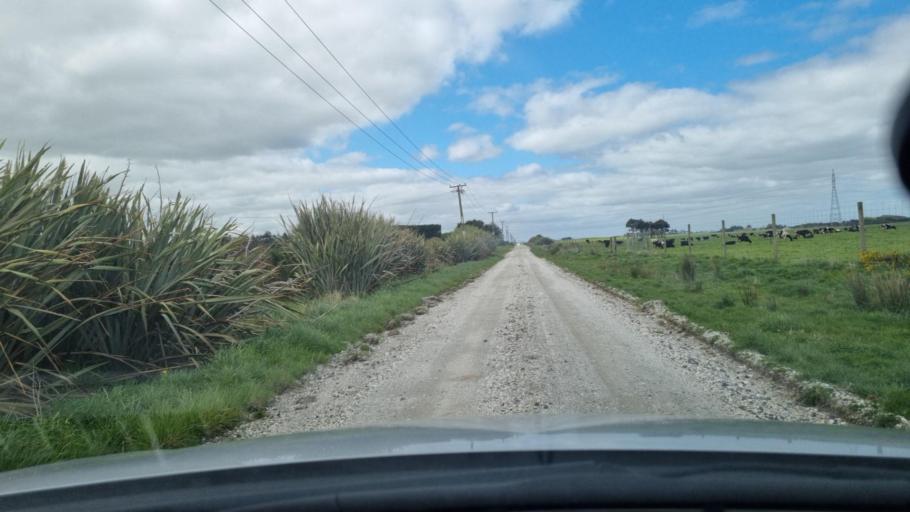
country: NZ
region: Southland
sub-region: Invercargill City
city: Invercargill
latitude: -46.4428
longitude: 168.4343
